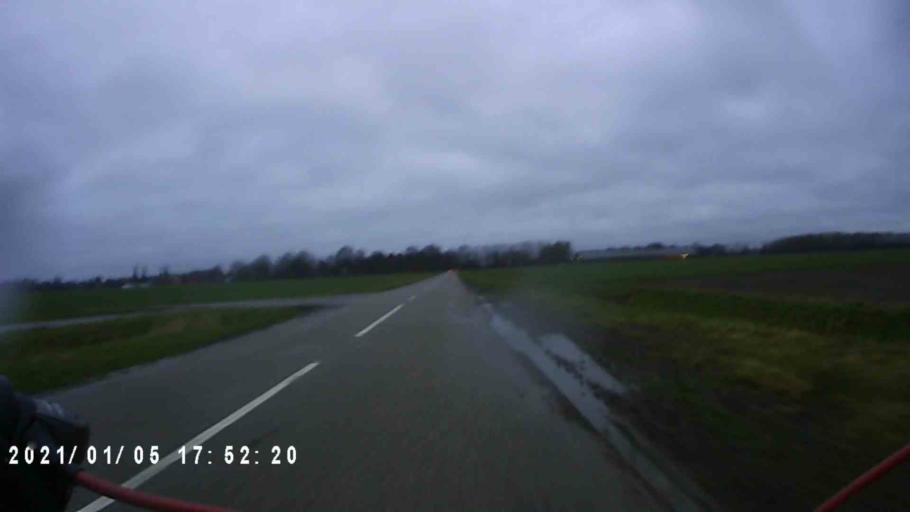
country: NL
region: Groningen
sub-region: Gemeente Slochteren
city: Slochteren
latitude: 53.2045
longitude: 6.8852
